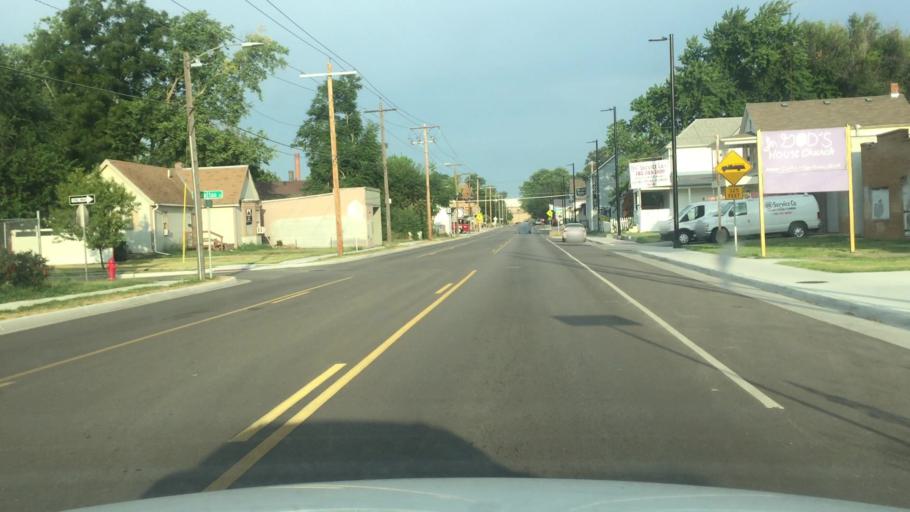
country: US
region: Kansas
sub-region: Shawnee County
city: Topeka
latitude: 39.0589
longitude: -95.6489
